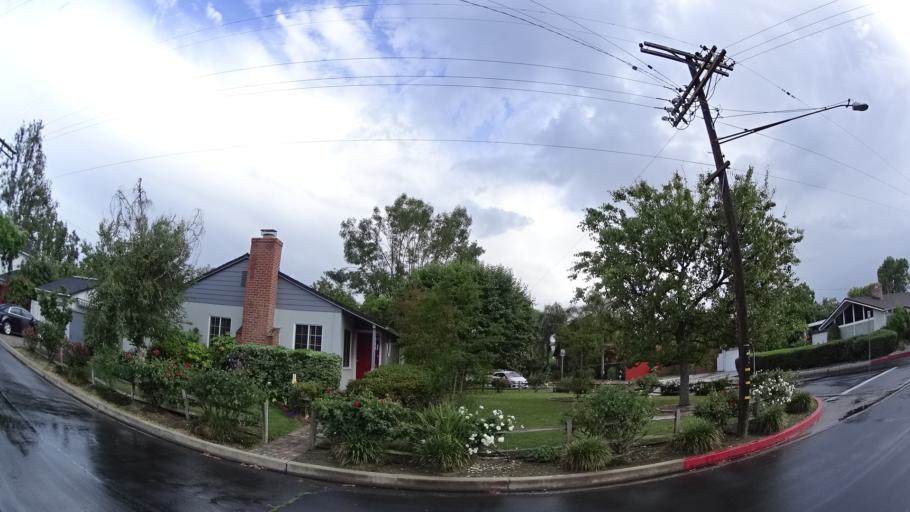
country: US
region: California
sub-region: Los Angeles County
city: Sherman Oaks
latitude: 34.1613
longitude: -118.4353
